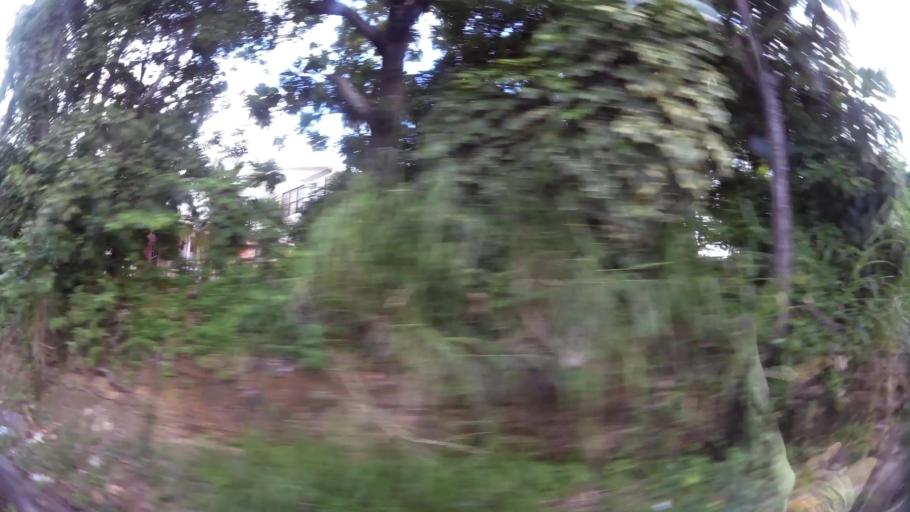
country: DM
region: Saint Paul
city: Mahaut
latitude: 15.3377
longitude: -61.3870
